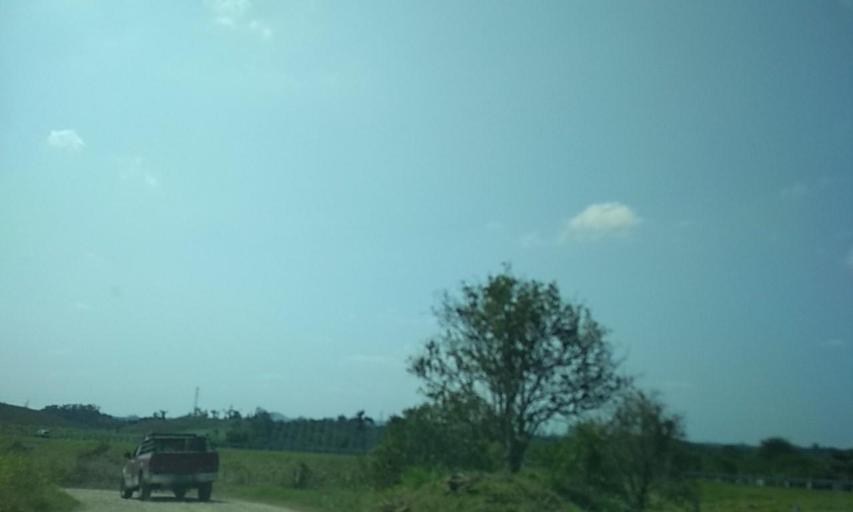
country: MX
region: Veracruz
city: Gutierrez Zamora
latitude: 20.3712
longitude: -97.1488
